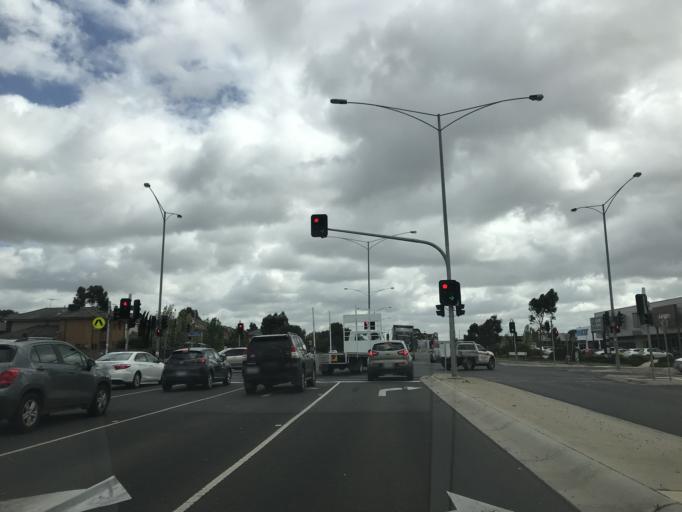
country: AU
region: Victoria
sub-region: Brimbank
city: Derrimut
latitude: -37.7834
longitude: 144.7729
